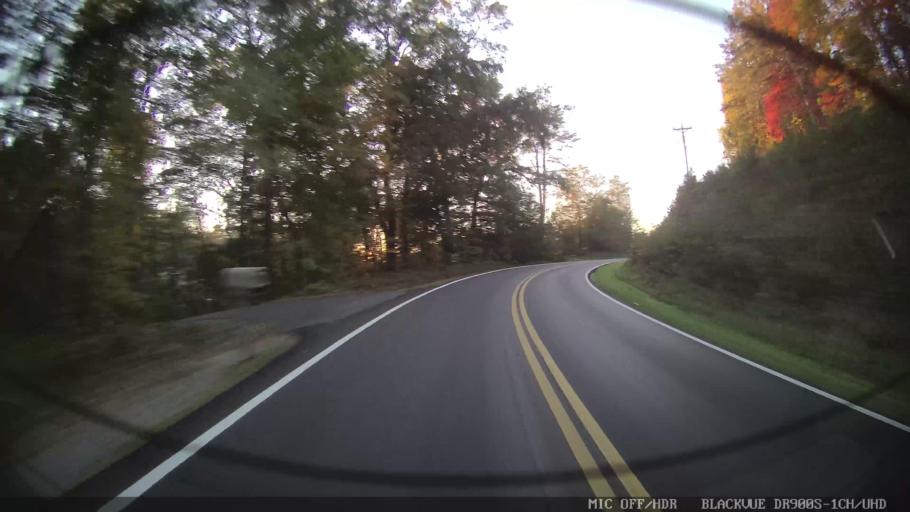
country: US
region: Georgia
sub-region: Union County
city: Blairsville
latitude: 34.8534
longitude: -83.9070
